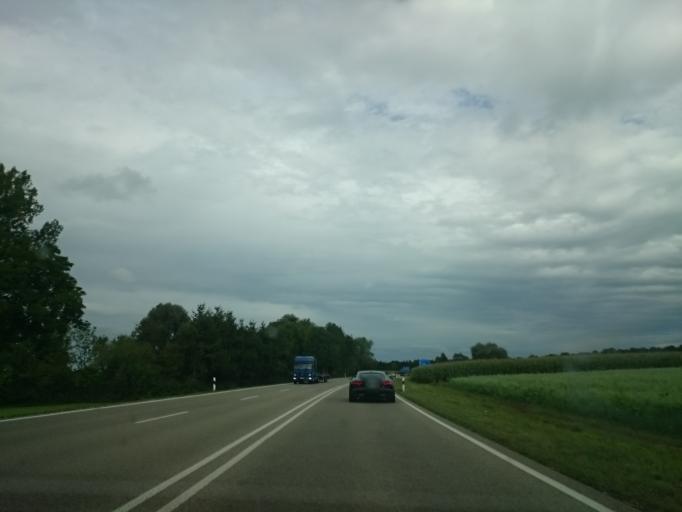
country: DE
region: Bavaria
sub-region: Swabia
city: Buchloe
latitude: 48.0200
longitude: 10.7230
